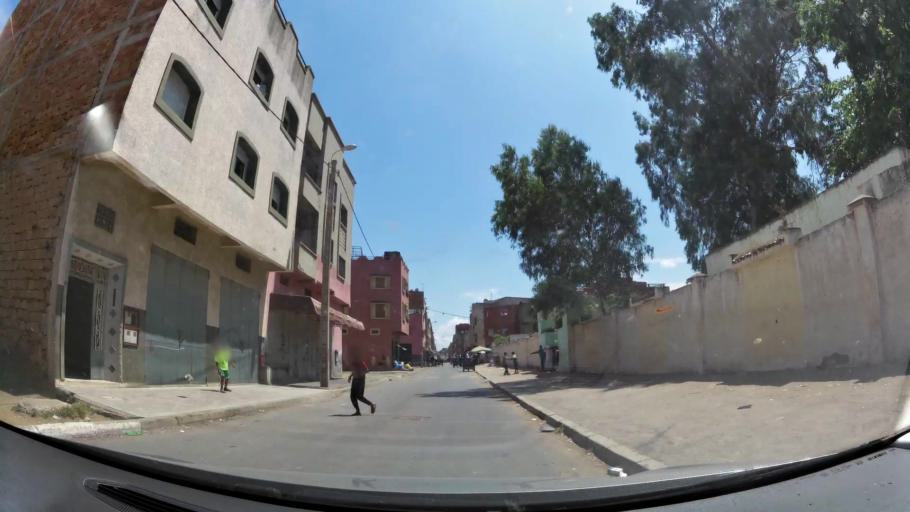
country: MA
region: Gharb-Chrarda-Beni Hssen
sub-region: Kenitra Province
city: Kenitra
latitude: 34.2532
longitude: -6.5551
